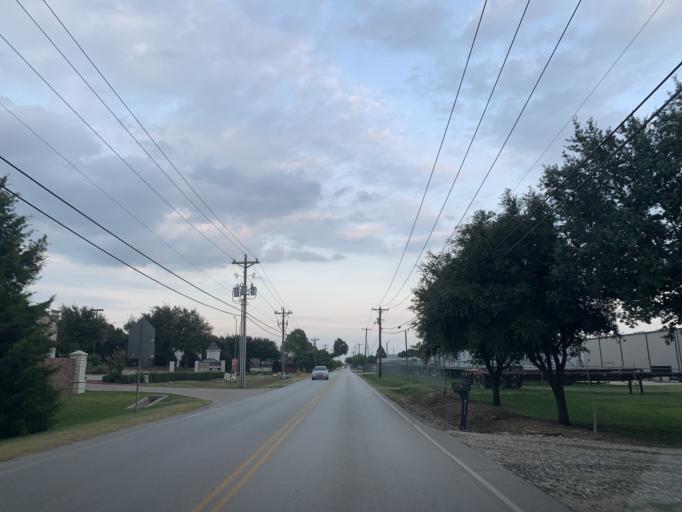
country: US
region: Texas
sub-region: Tarrant County
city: Keller
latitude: 32.9388
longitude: -97.2683
